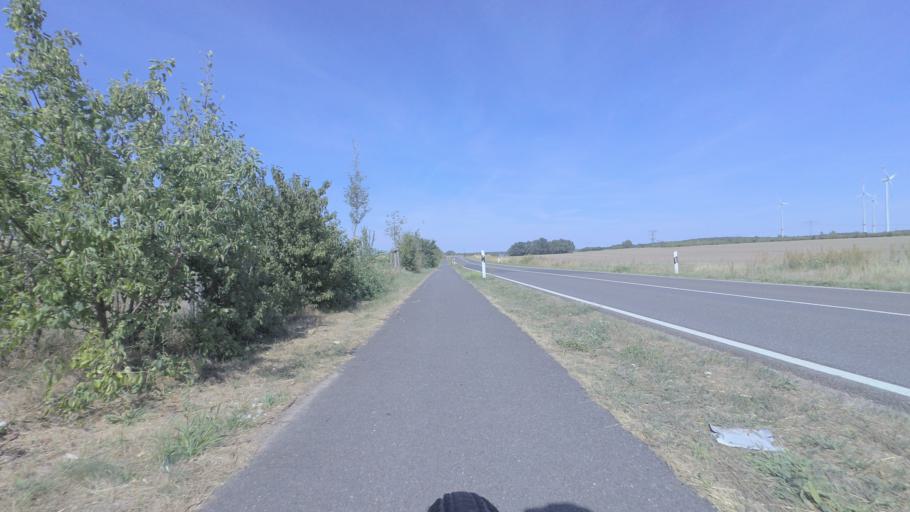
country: DE
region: Brandenburg
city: Trebbin
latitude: 52.2065
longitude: 13.2791
